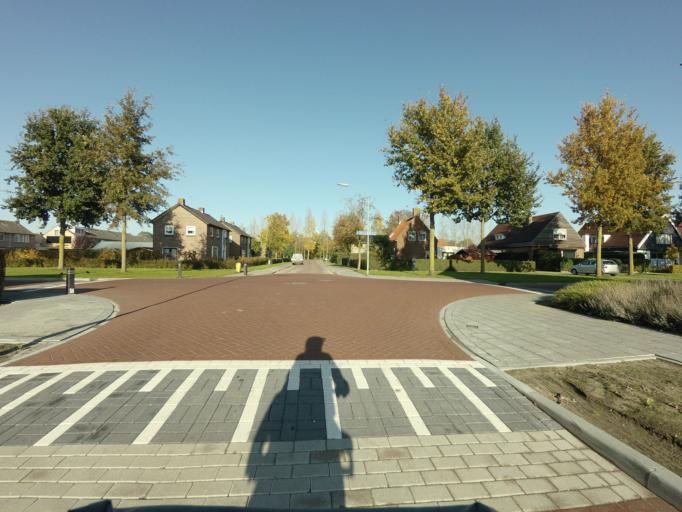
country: NL
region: North Brabant
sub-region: Gemeente Woudrichem
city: Almkerk
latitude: 51.7334
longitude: 4.9605
